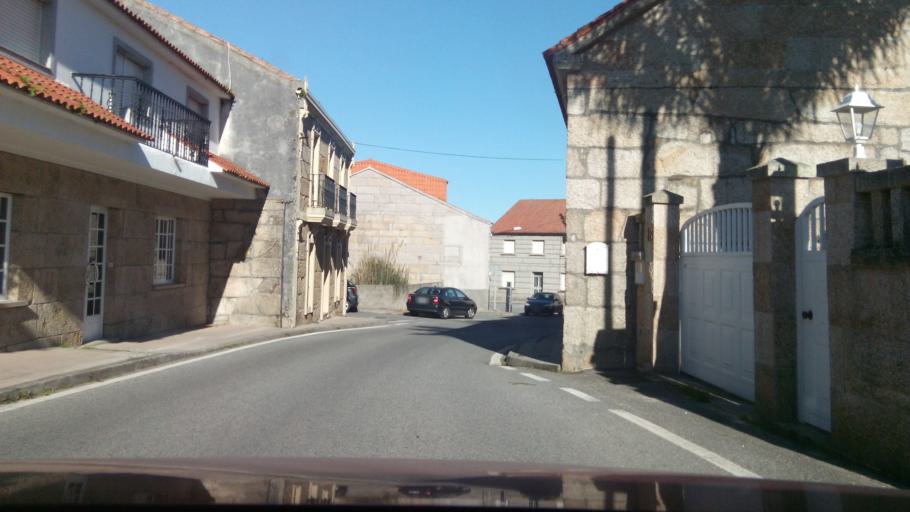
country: ES
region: Galicia
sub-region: Provincia de Pontevedra
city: O Grove
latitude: 42.4680
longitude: -8.9263
